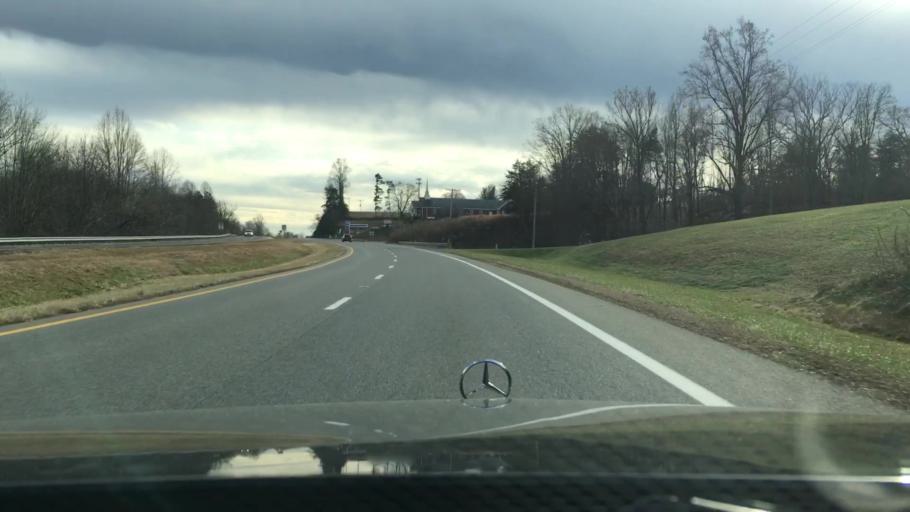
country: US
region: Virginia
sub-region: Pittsylvania County
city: Motley
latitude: 37.0273
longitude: -79.3588
